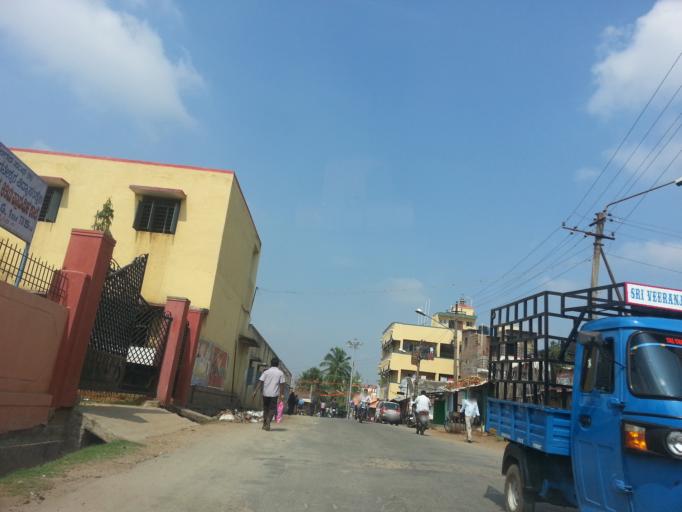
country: IN
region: Karnataka
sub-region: Mysore
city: Mysore
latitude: 12.3354
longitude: 76.6638
